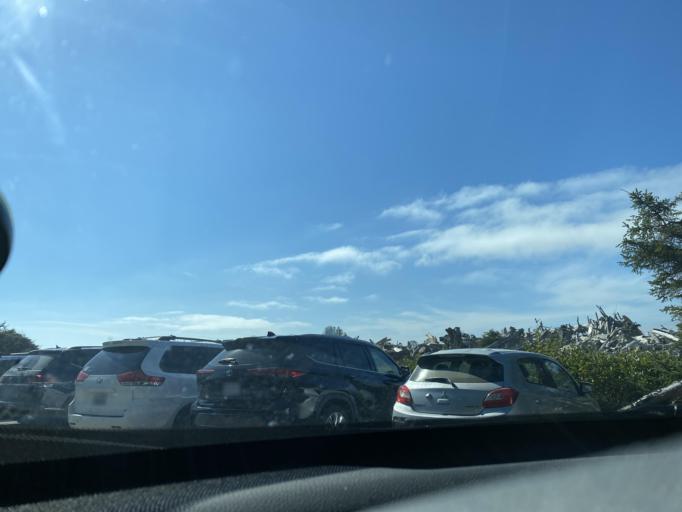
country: US
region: Washington
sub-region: Clallam County
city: Forks
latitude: 47.9208
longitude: -124.6379
